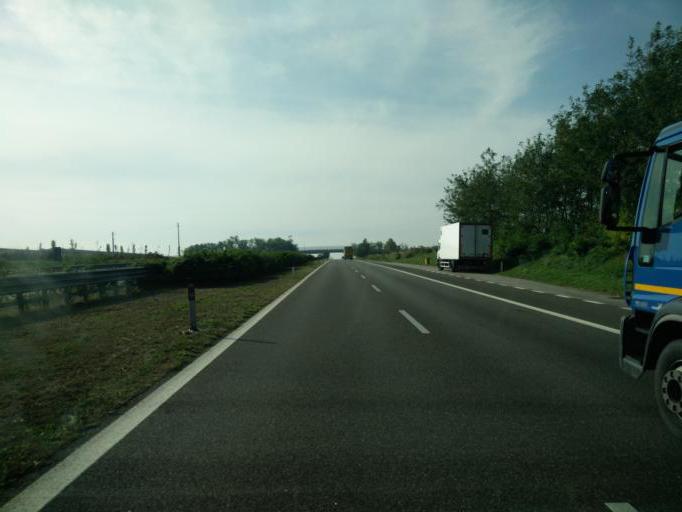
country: IT
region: Lombardy
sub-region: Provincia di Cremona
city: Corte de' Frati
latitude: 45.2401
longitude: 10.1189
